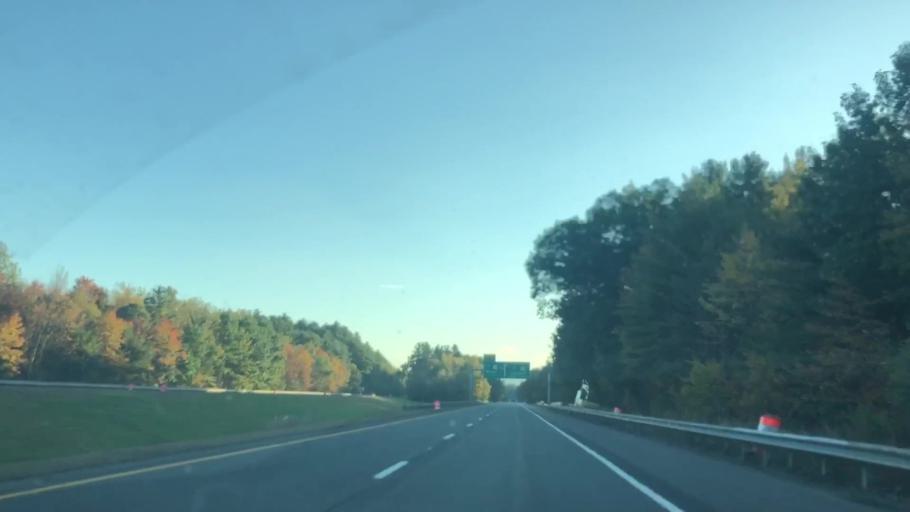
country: US
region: Massachusetts
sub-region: Franklin County
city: Turners Falls
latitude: 42.6329
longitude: -72.5798
